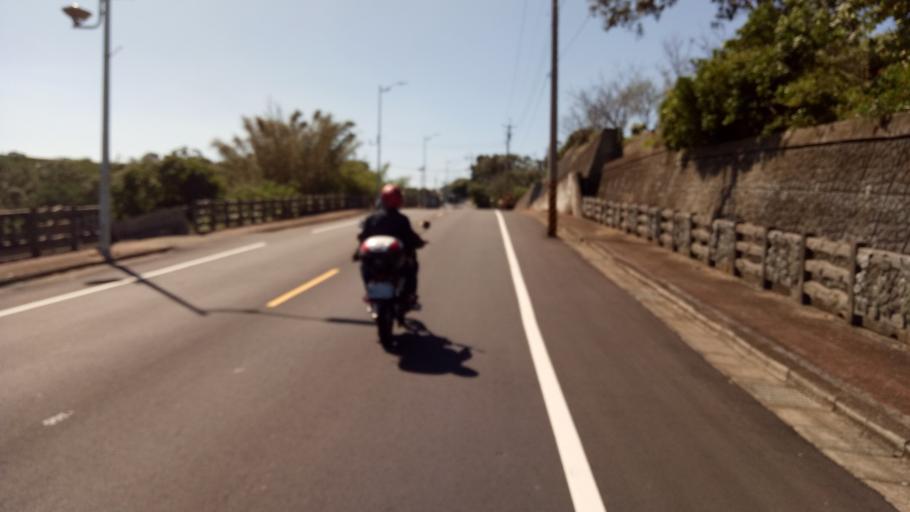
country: TW
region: Taiwan
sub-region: Hsinchu
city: Hsinchu
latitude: 24.7165
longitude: 120.9231
